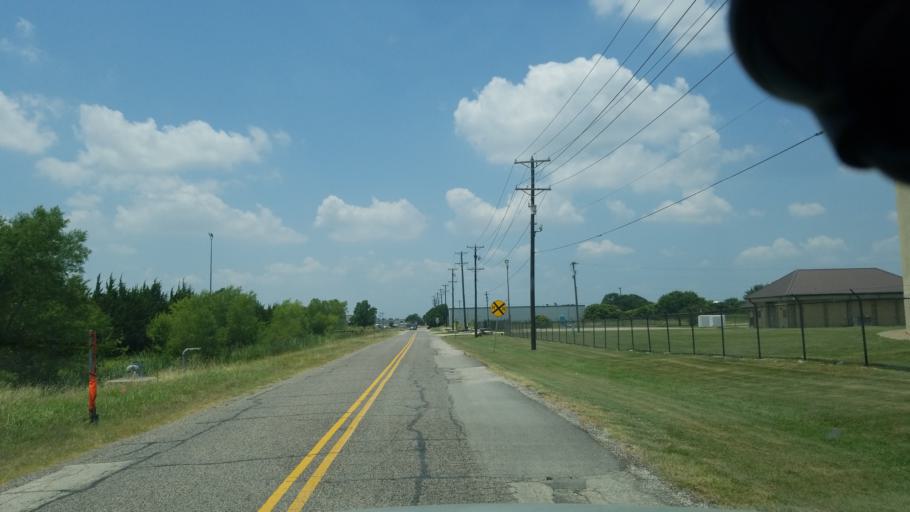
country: US
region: Texas
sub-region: Dallas County
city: Carrollton
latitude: 32.9599
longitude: -96.8729
